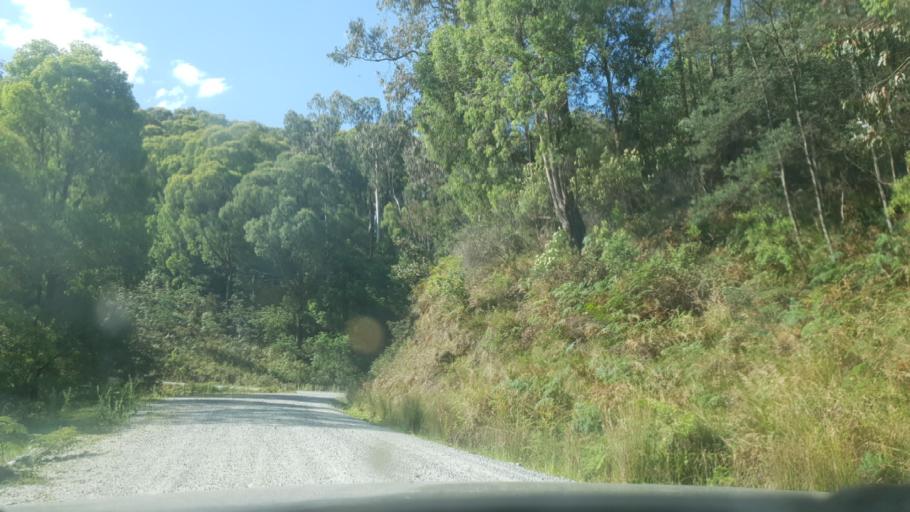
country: AU
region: Victoria
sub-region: Alpine
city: Mount Beauty
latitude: -36.7514
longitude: 147.1865
